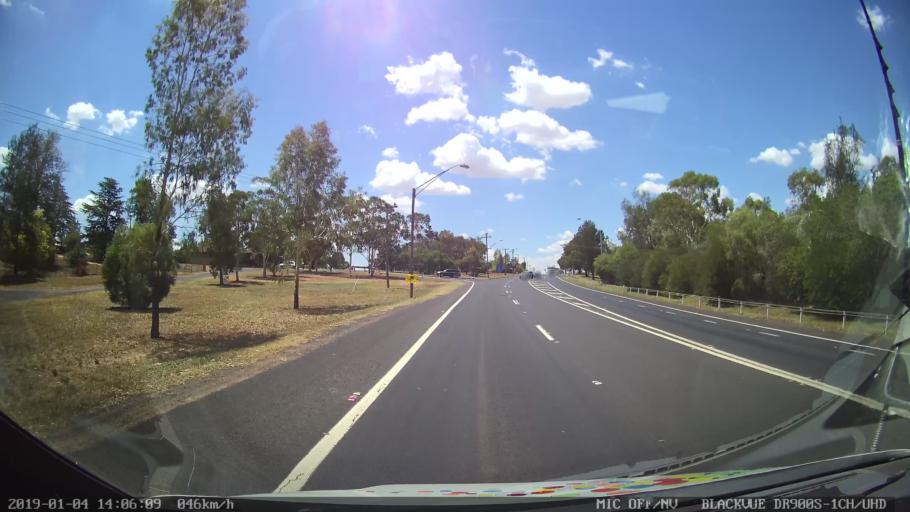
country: AU
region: New South Wales
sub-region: Dubbo Municipality
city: Dubbo
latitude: -32.2569
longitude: 148.5865
